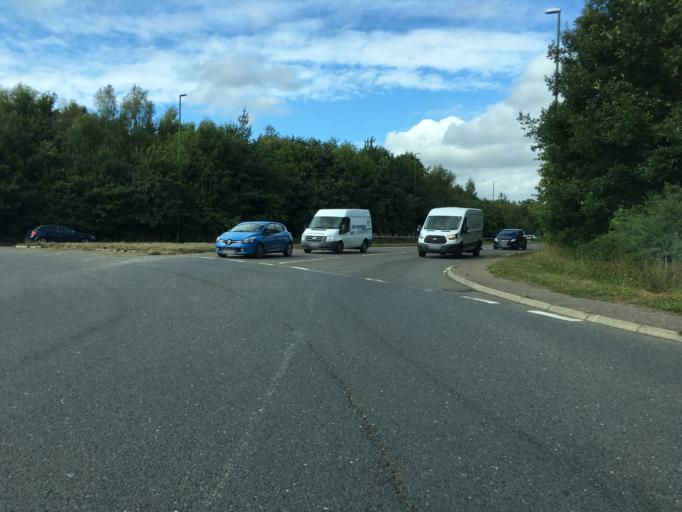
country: GB
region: England
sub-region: West Sussex
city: Horsham
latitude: 51.0792
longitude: -0.3372
